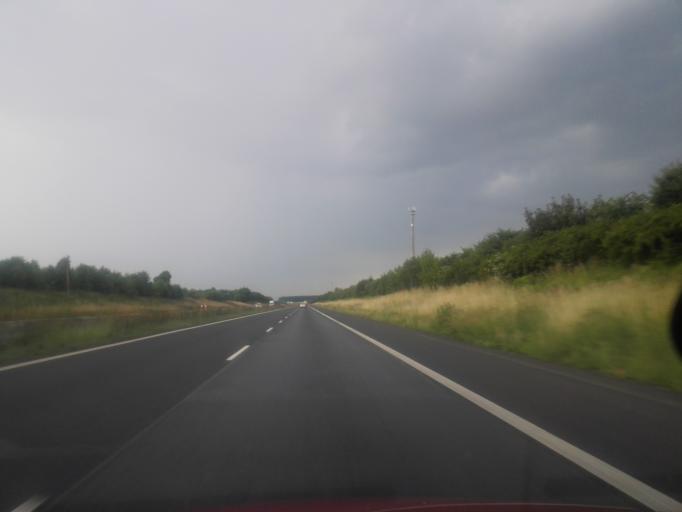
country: PL
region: Silesian Voivodeship
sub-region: Powiat czestochowski
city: Borowno
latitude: 50.9645
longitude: 19.2583
